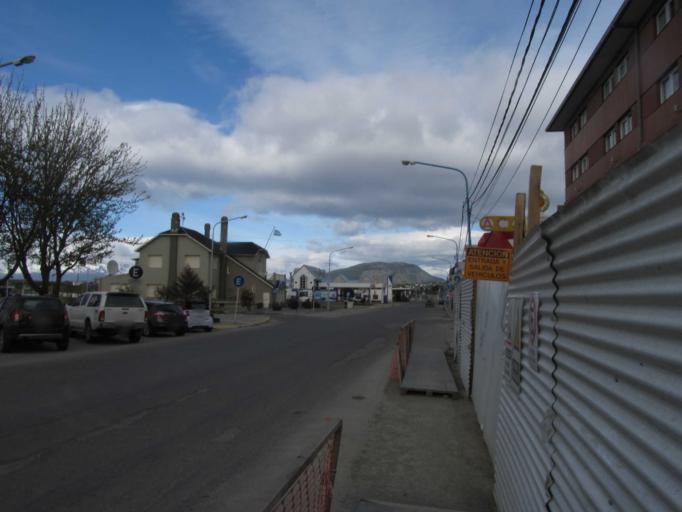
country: AR
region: Tierra del Fuego
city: Ushuaia
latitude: -54.8073
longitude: -68.3052
